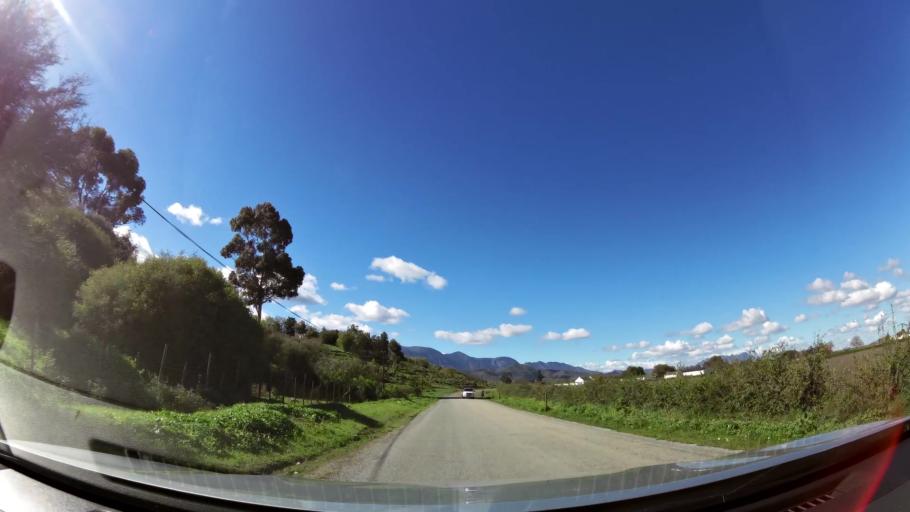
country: ZA
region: Western Cape
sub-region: Cape Winelands District Municipality
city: Ashton
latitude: -33.7946
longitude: 19.8970
